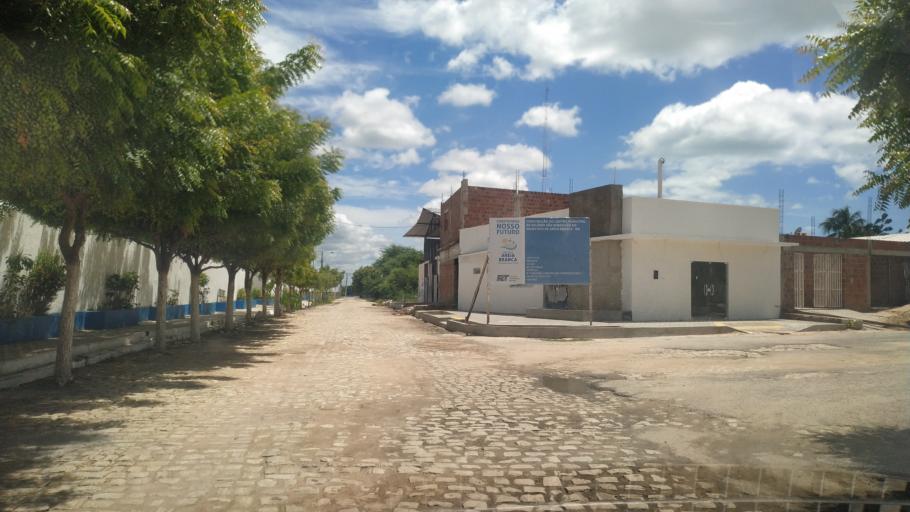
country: BR
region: Rio Grande do Norte
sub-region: Areia Branca
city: Areia Branca
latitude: -4.9594
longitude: -37.1359
